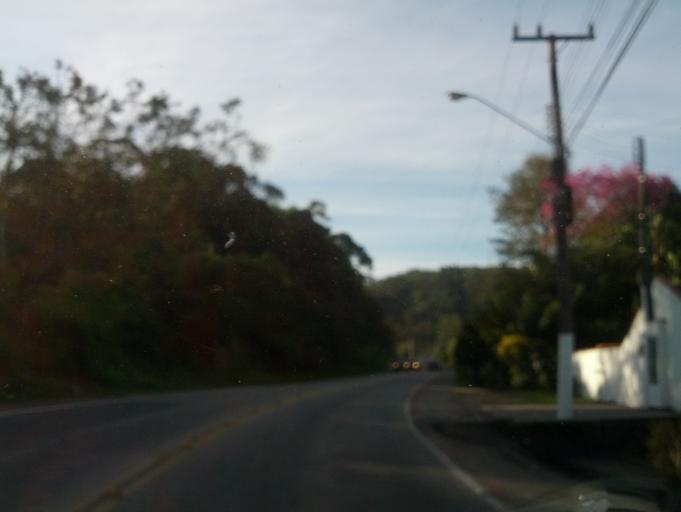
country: BR
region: Santa Catarina
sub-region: Indaial
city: Indaial
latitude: -26.8833
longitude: -49.1759
